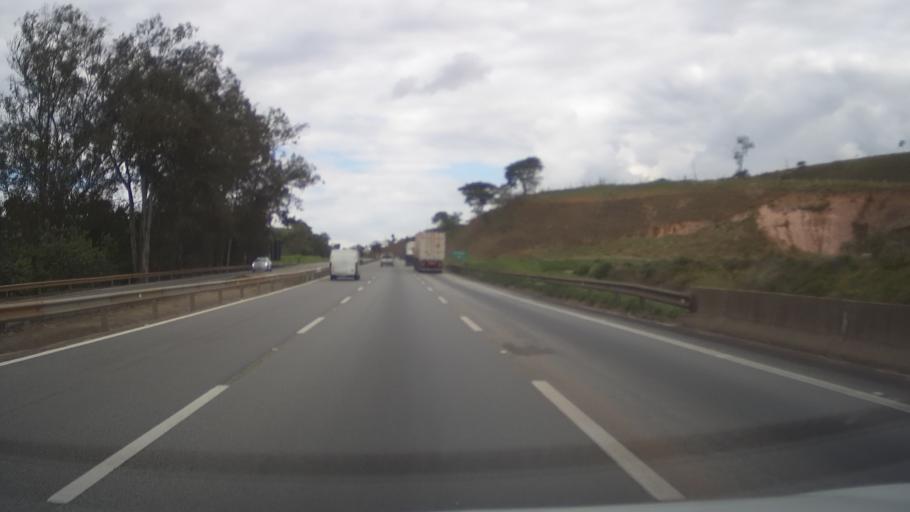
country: BR
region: Minas Gerais
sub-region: Itauna
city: Itauna
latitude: -20.3492
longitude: -44.4442
